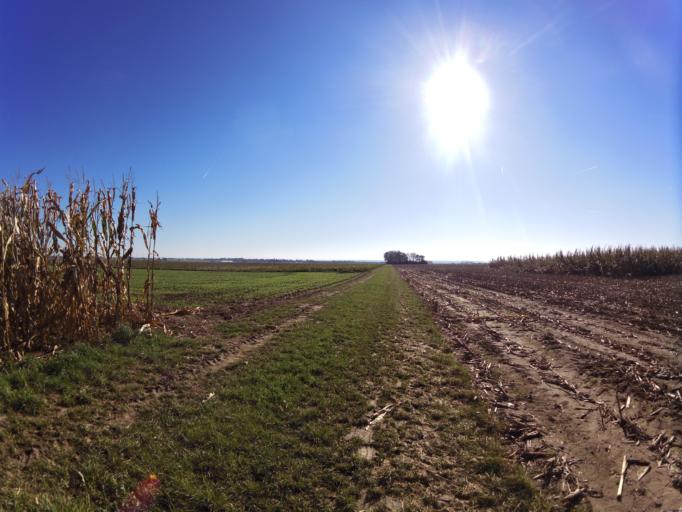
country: DE
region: Bavaria
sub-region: Regierungsbezirk Unterfranken
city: Giebelstadt
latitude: 49.6735
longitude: 9.9336
